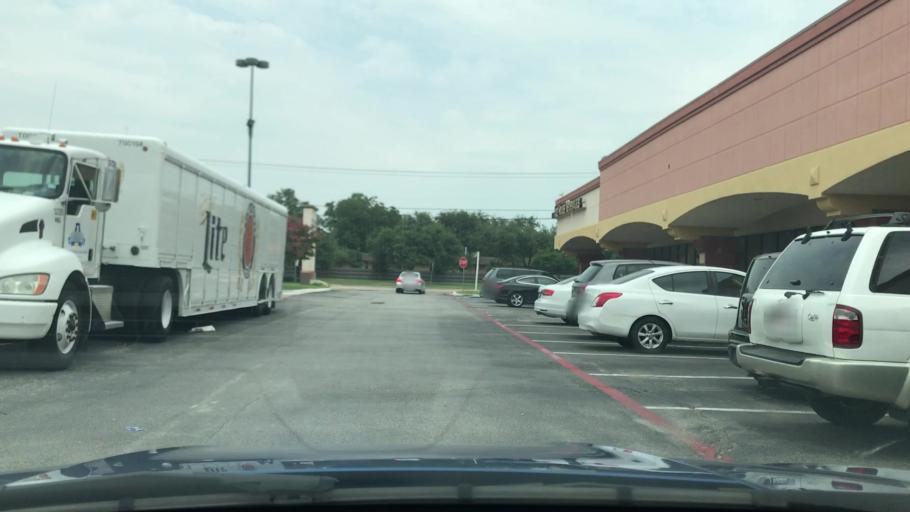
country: US
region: Texas
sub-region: Dallas County
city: Richardson
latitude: 32.9614
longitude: -96.7678
